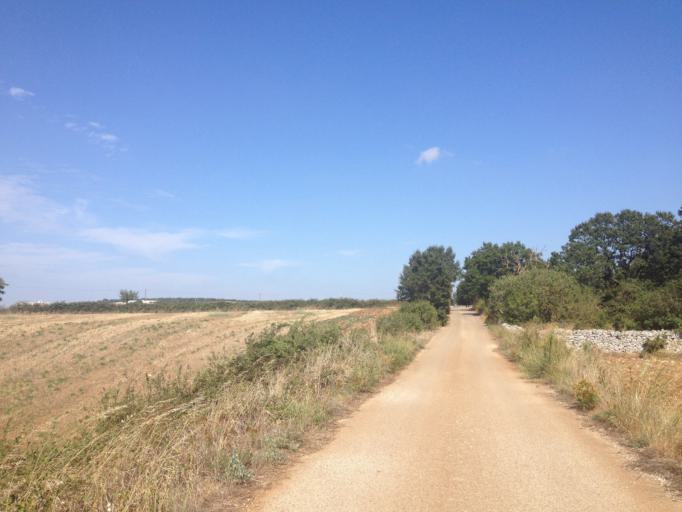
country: IT
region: Apulia
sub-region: Provincia di Bari
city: Sammichele di Bari
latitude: 40.8231
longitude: 17.0111
